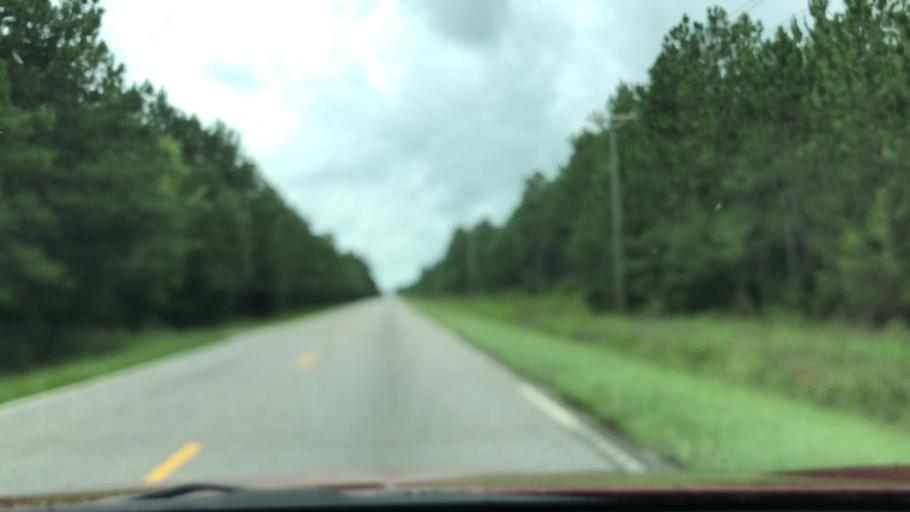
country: US
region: South Carolina
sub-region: Georgetown County
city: Murrells Inlet
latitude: 33.5808
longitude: -79.2075
